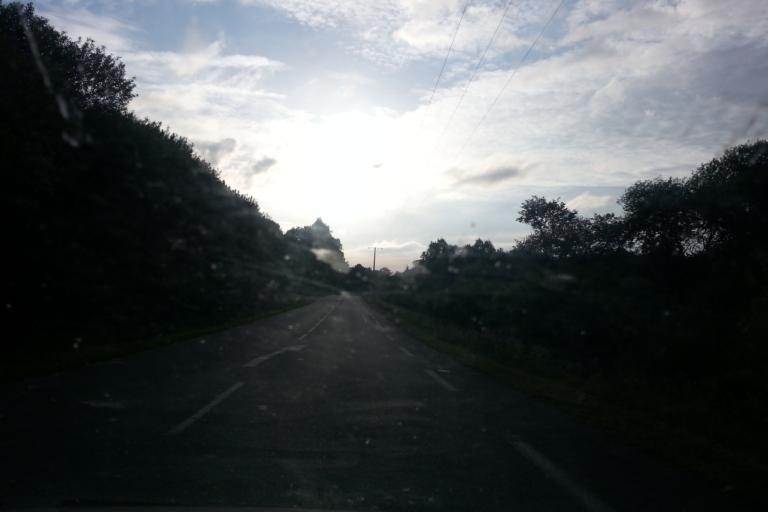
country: FR
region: Brittany
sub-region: Departement du Morbihan
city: Plouray
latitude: 48.1364
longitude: -3.3531
